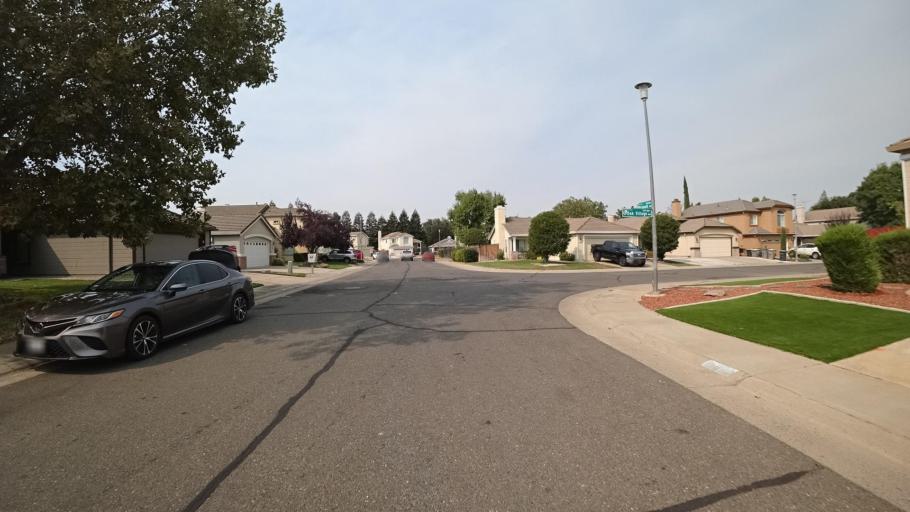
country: US
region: California
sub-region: Sacramento County
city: Laguna
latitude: 38.4128
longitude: -121.4045
